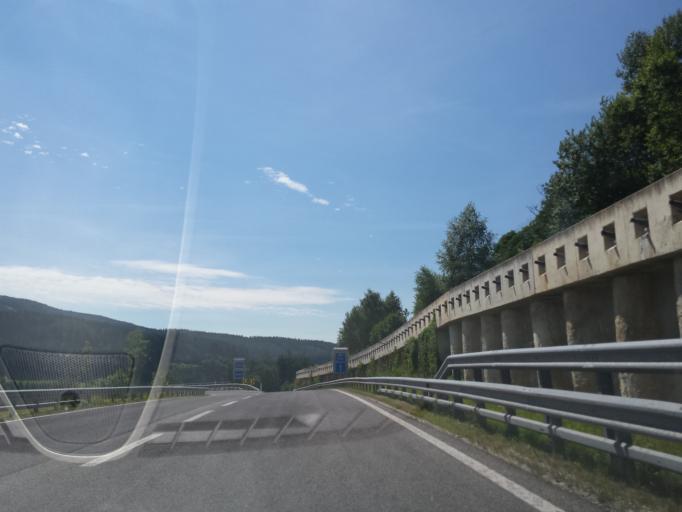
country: AT
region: Styria
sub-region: Politischer Bezirk Bruck-Muerzzuschlag
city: Spital am Semmering
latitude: 47.6198
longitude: 15.7748
